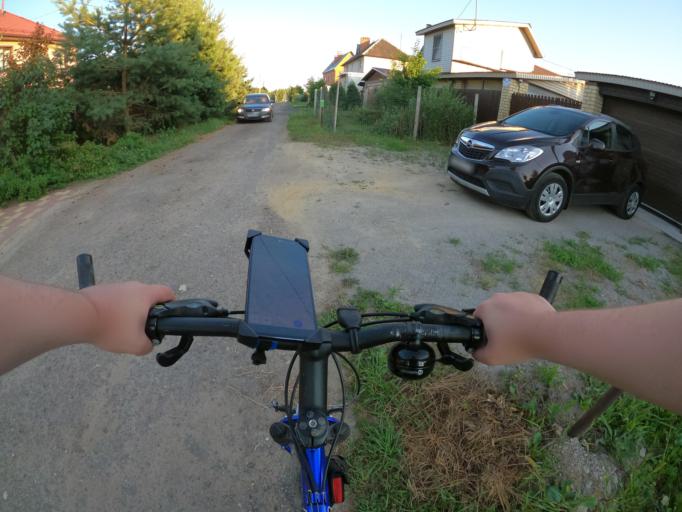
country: RU
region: Moskovskaya
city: Beloozerskiy
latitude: 55.4627
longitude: 38.4239
